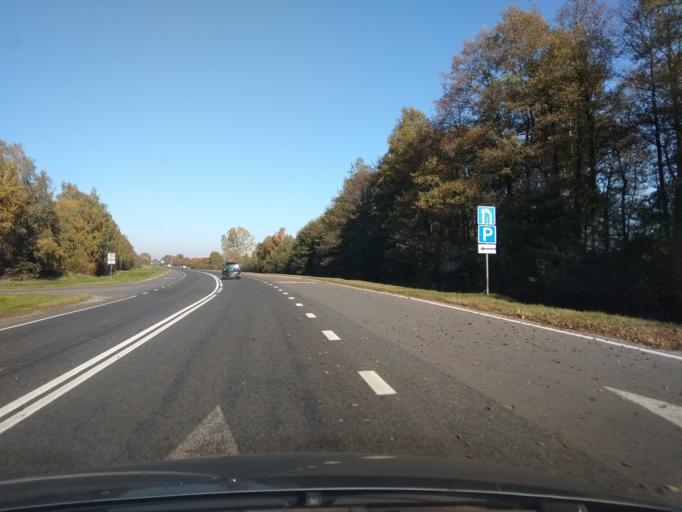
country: BY
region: Brest
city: Kobryn
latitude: 52.1437
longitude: 24.3121
